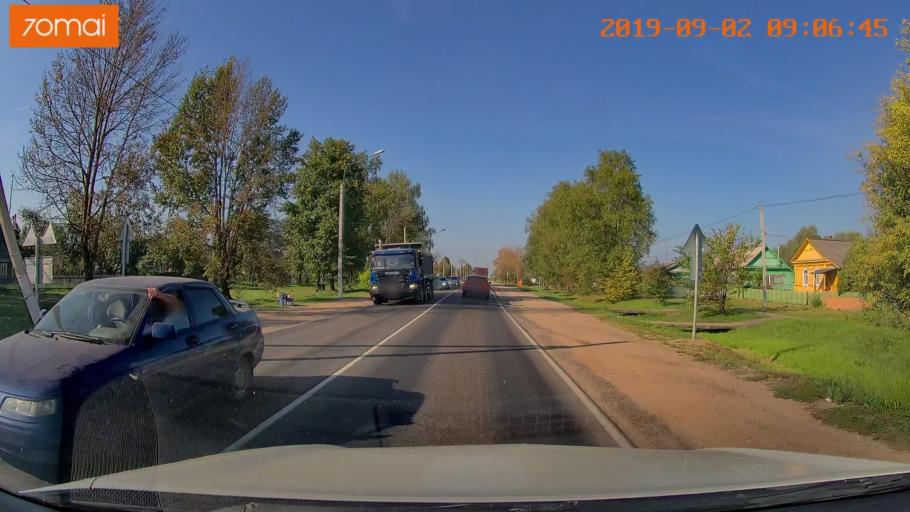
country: RU
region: Kaluga
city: Myatlevo
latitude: 54.8987
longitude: 35.6662
